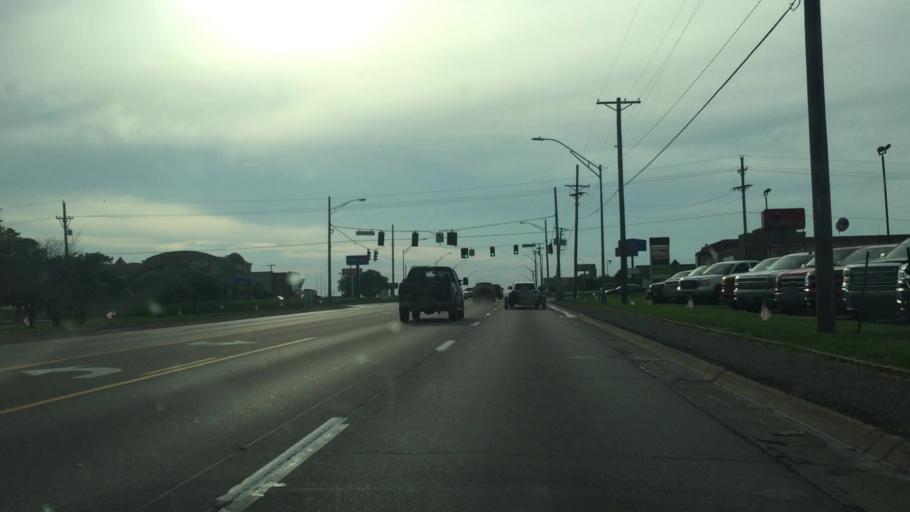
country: US
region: Missouri
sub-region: Pettis County
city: Sedalia
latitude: 38.7100
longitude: -93.2691
